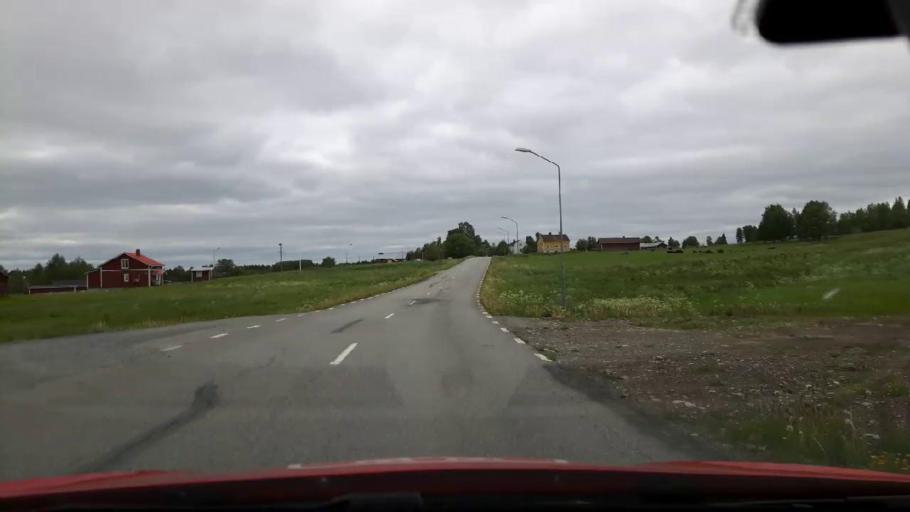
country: SE
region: Jaemtland
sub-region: Stroemsunds Kommun
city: Stroemsund
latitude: 63.5583
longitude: 15.4013
